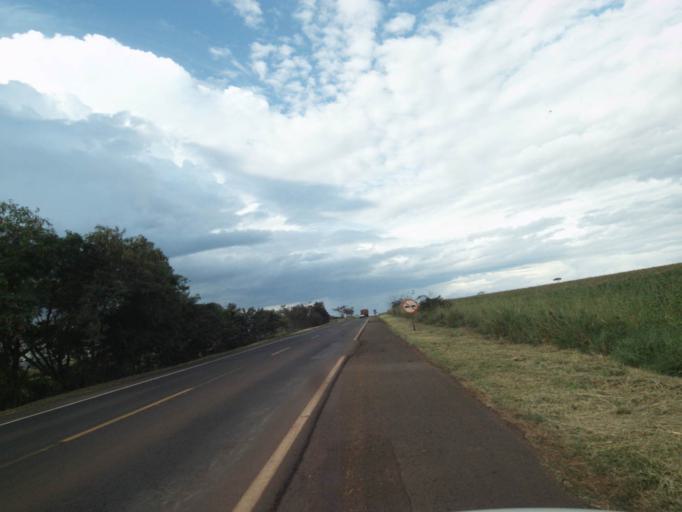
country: PY
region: Canindeyu
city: Salto del Guaira
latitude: -24.0847
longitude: -54.0772
